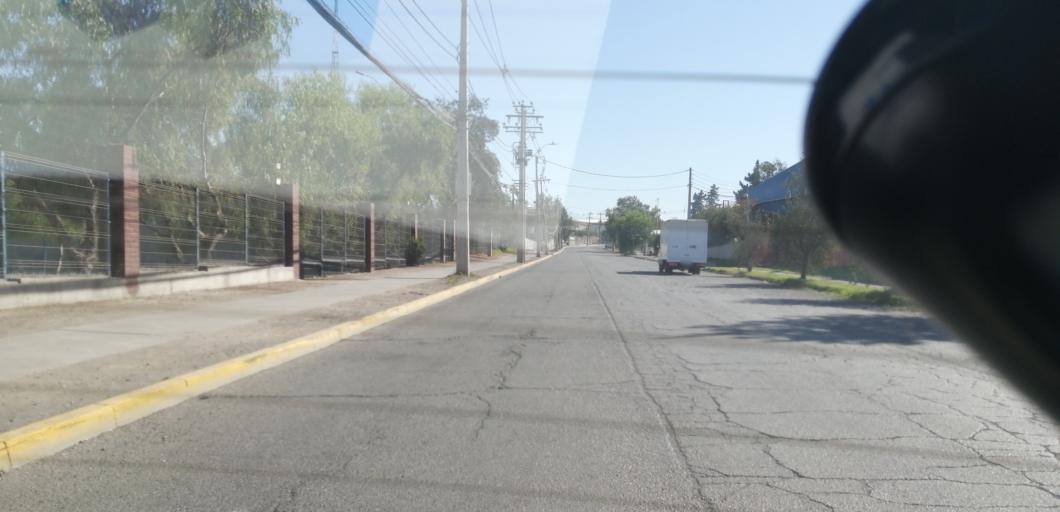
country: CL
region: Santiago Metropolitan
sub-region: Provincia de Santiago
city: Lo Prado
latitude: -33.4503
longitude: -70.7841
